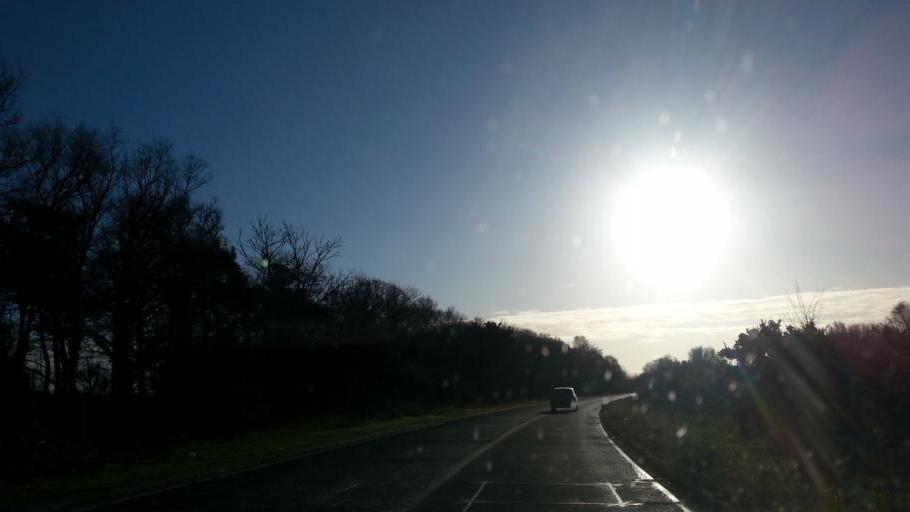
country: GB
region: England
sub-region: Suffolk
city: Felixstowe
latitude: 51.9931
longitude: 1.3163
